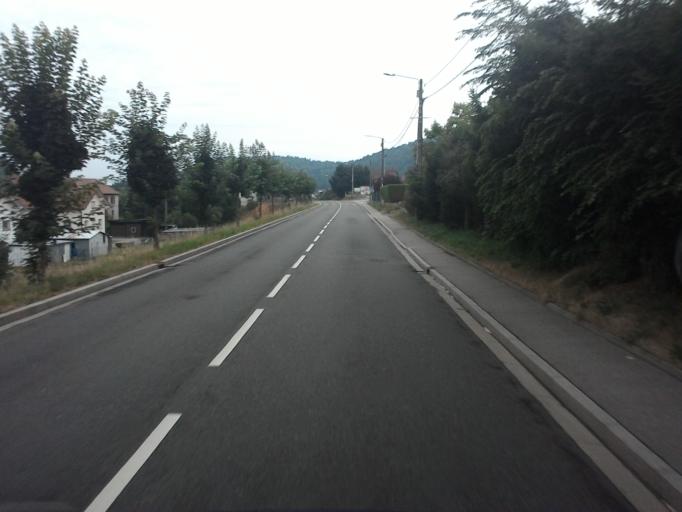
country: FR
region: Lorraine
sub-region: Departement des Vosges
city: Fresse-sur-Moselle
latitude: 47.8707
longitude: 6.7930
